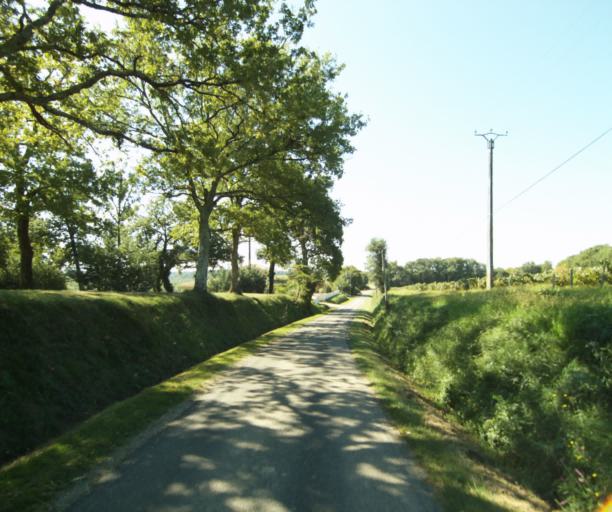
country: FR
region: Midi-Pyrenees
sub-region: Departement du Gers
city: Cazaubon
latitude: 43.9376
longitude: -0.0165
